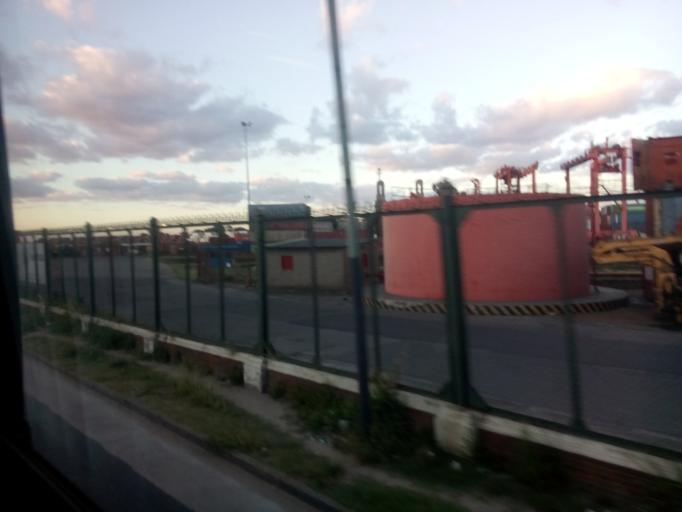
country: AR
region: Buenos Aires F.D.
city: Retiro
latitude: -34.5787
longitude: -58.3821
